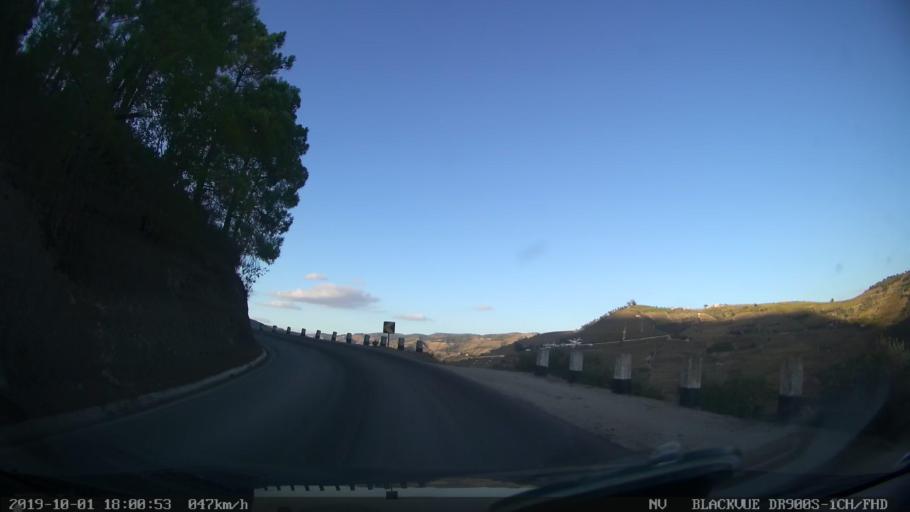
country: PT
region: Vila Real
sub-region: Sabrosa
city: Vilela
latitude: 41.2027
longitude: -7.5478
